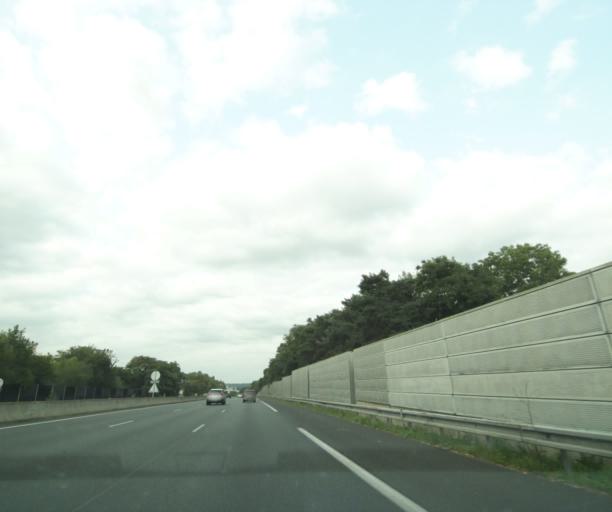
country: FR
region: Centre
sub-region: Departement d'Indre-et-Loire
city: Chambray-les-Tours
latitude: 47.3590
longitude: 0.7103
